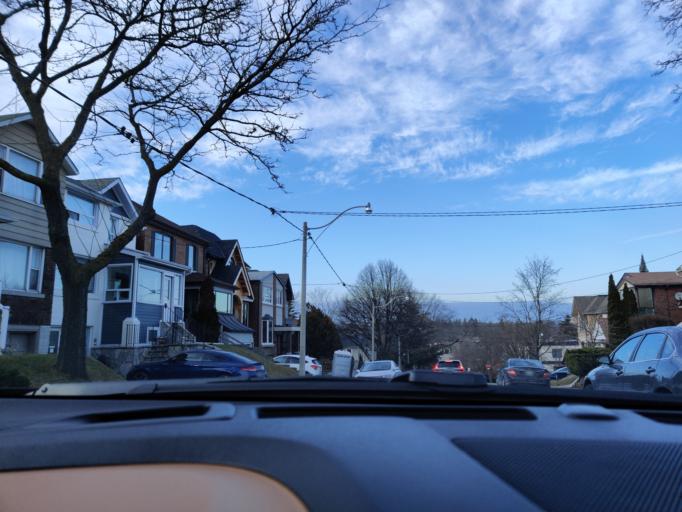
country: CA
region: Ontario
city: Toronto
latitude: 43.7105
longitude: -79.3824
